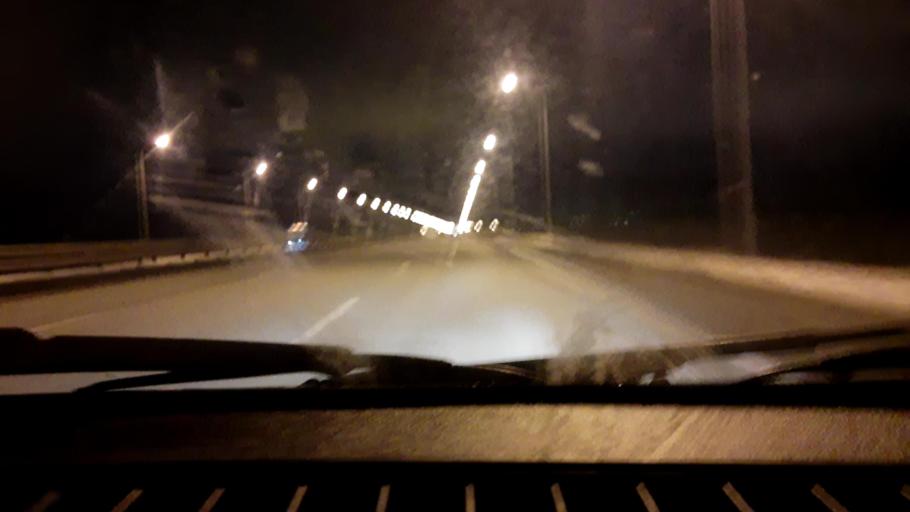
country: RU
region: Bashkortostan
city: Asanovo
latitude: 54.8900
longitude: 55.6561
